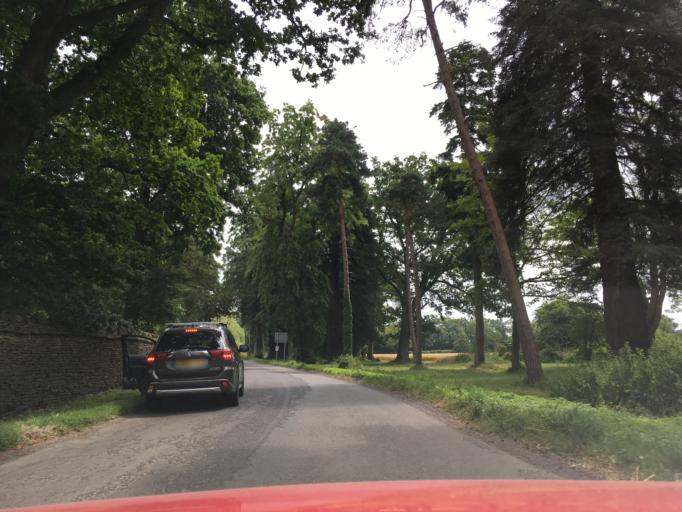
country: GB
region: England
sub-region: Oxfordshire
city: Hook Norton
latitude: 51.9551
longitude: -1.4220
